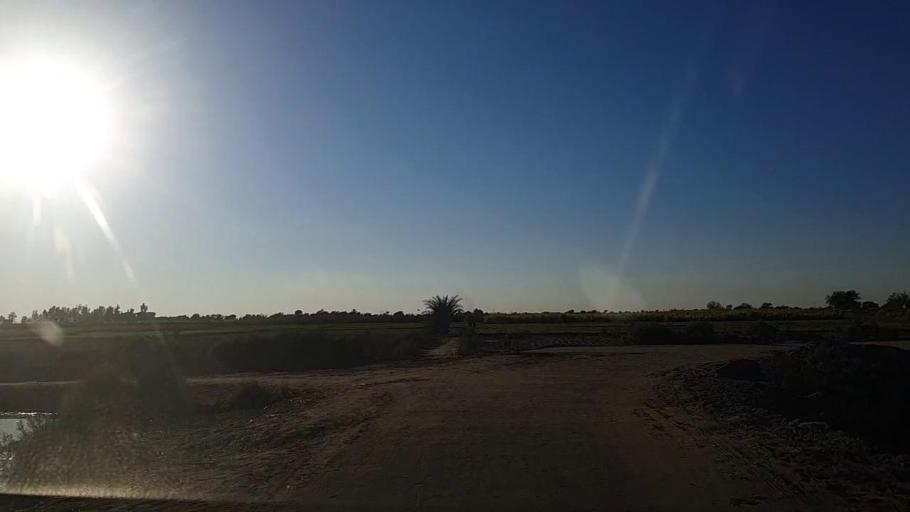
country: PK
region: Sindh
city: Sanghar
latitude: 26.1393
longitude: 68.9268
